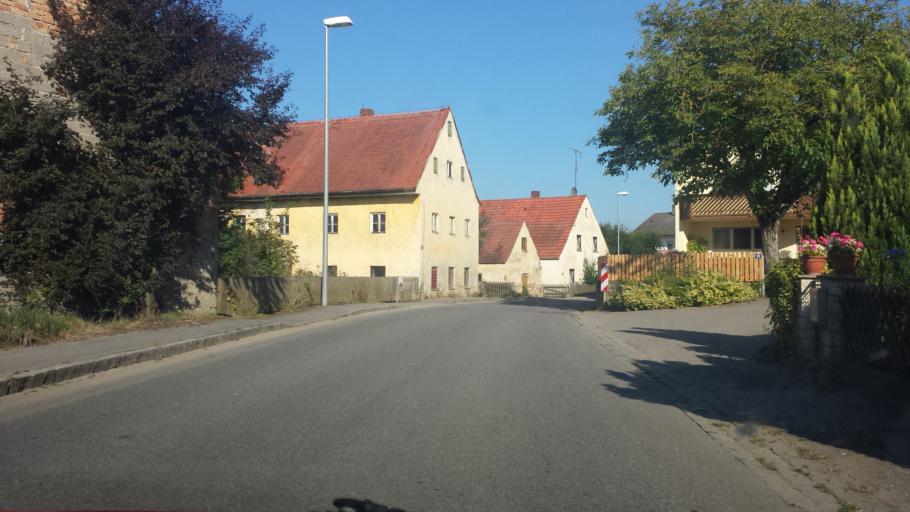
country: DE
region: Bavaria
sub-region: Lower Bavaria
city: Neustadt an der Donau
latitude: 48.8320
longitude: 11.7726
